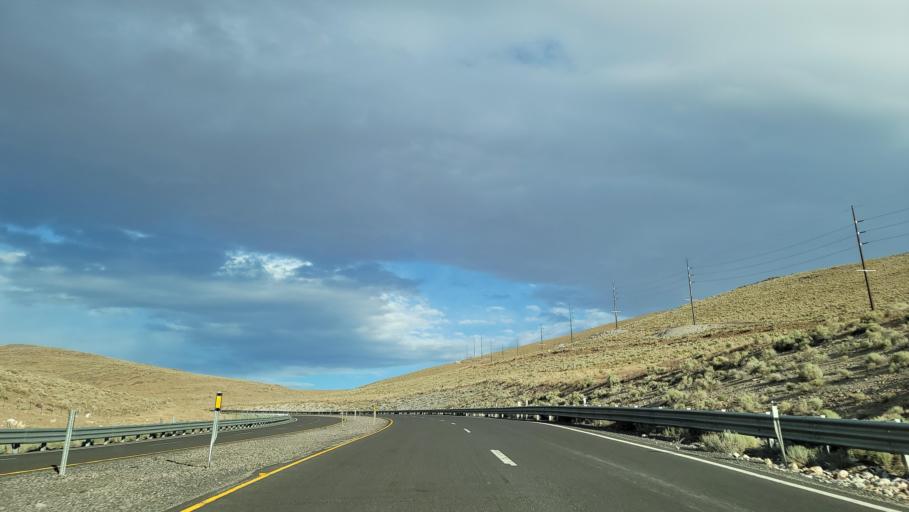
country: US
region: Nevada
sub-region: Lyon County
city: Stagecoach
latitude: 39.5108
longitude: -119.4649
